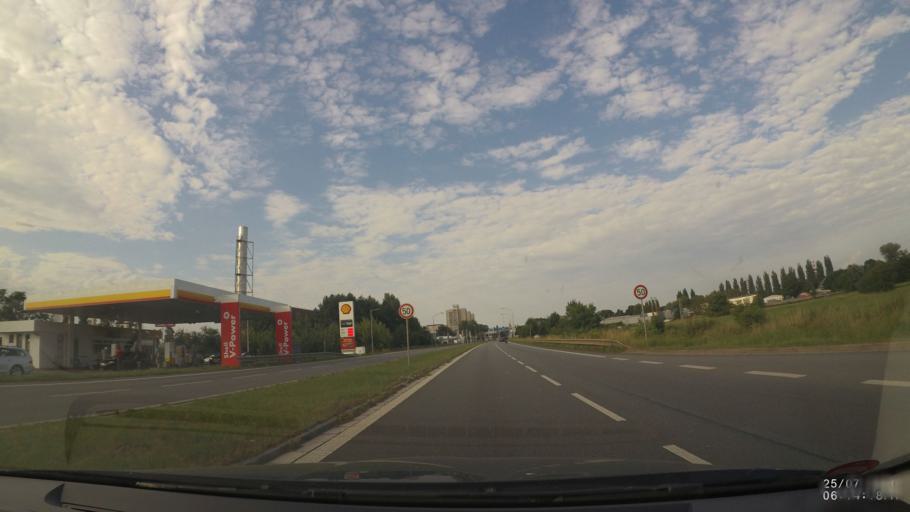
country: CZ
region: Kralovehradecky
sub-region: Okres Hradec Kralove
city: Hradec Kralove
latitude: 50.1940
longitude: 15.8111
